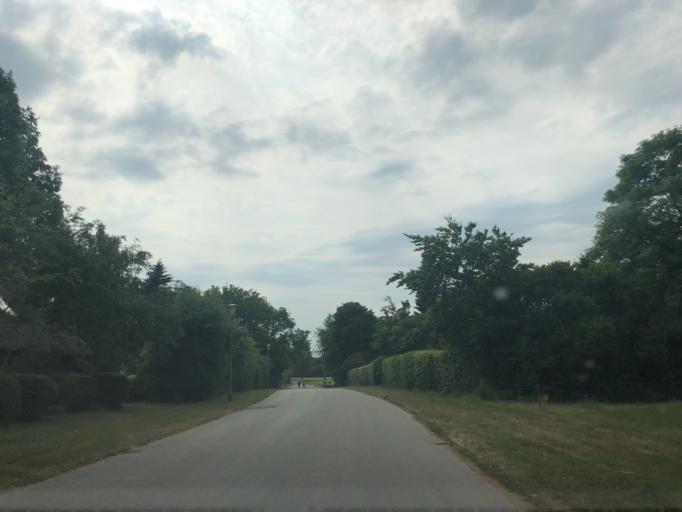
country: DK
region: Zealand
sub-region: Koge Kommune
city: Koge
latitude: 55.4564
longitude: 12.1649
